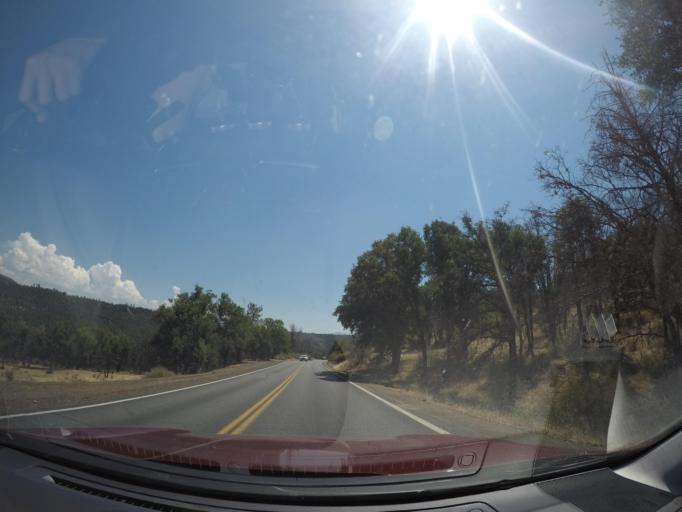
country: US
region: California
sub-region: Shasta County
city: Burney
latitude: 40.9921
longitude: -121.5125
